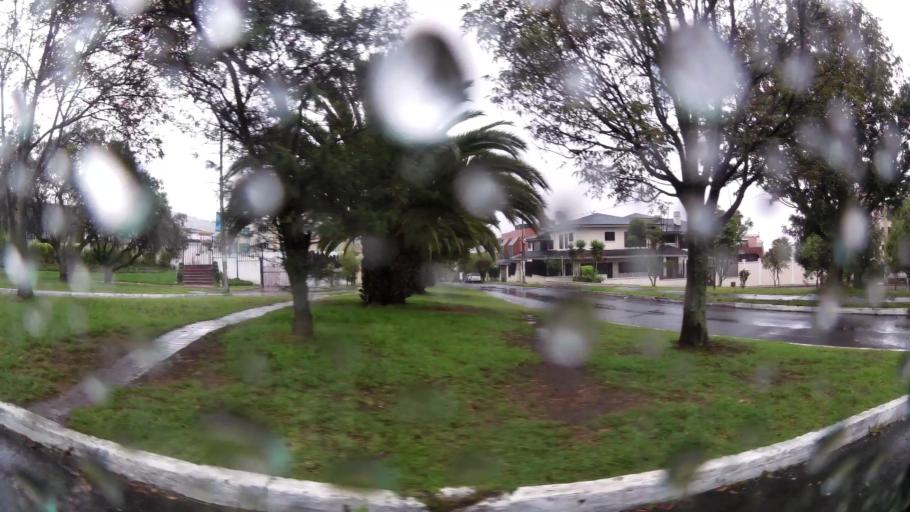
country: EC
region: Pichincha
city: Quito
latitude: -0.1026
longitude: -78.5006
